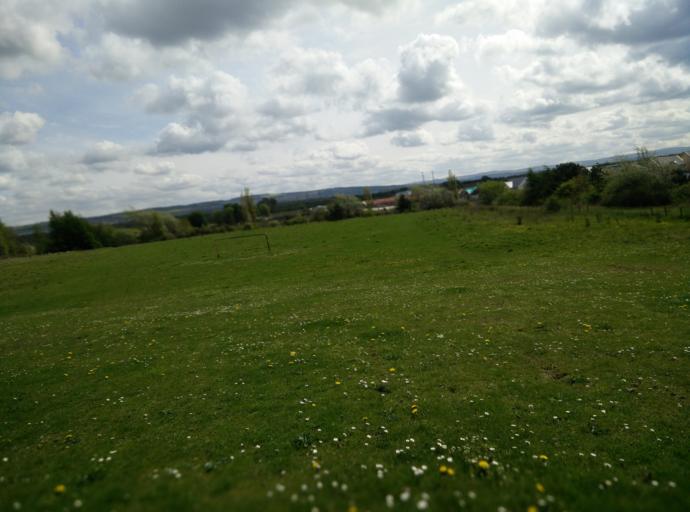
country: GB
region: Scotland
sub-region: Midlothian
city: Dalkeith
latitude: 55.9156
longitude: -3.1032
